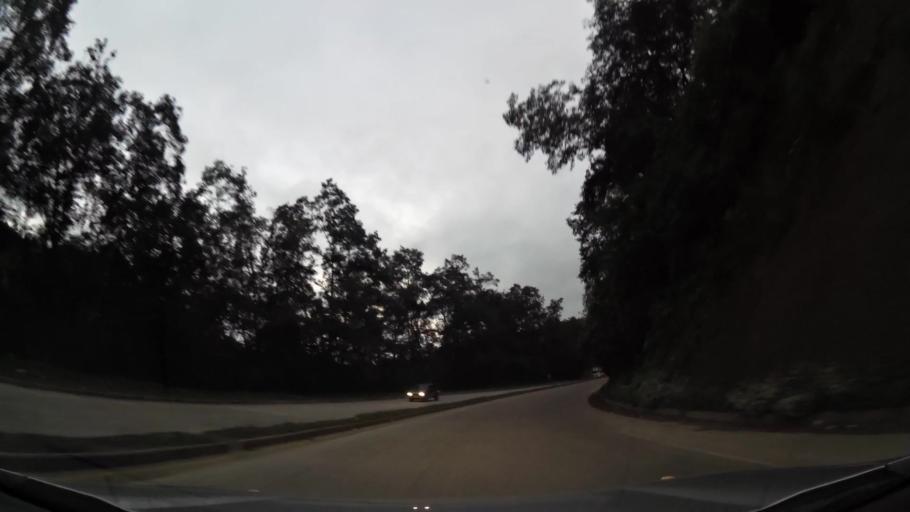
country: GT
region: Chimaltenango
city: Santa Apolonia
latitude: 14.8448
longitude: -91.0480
